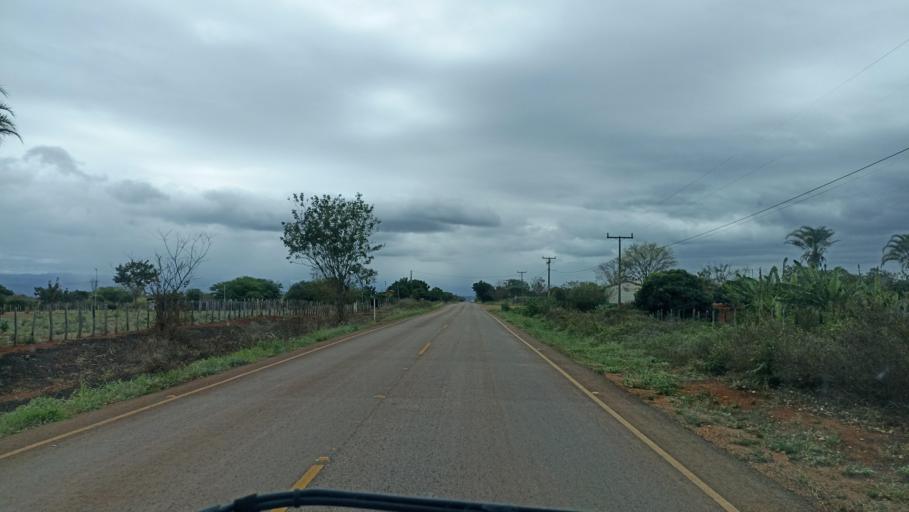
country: BR
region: Bahia
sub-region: Andarai
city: Vera Cruz
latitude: -12.9717
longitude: -41.0258
